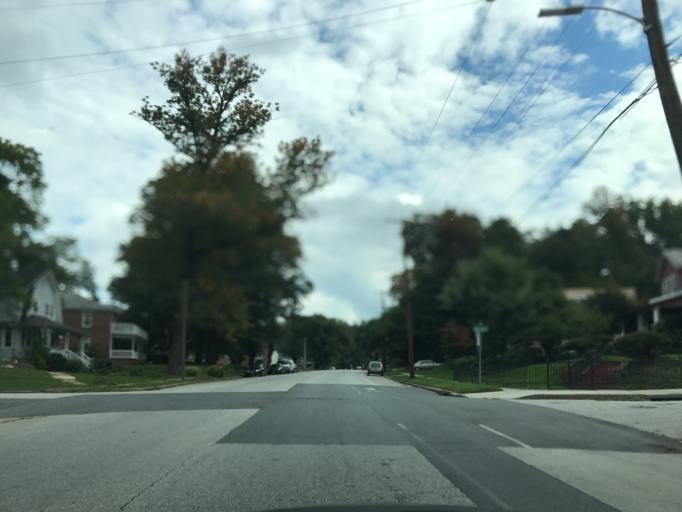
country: US
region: Maryland
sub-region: Baltimore County
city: Lochearn
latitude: 39.3273
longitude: -76.7111
